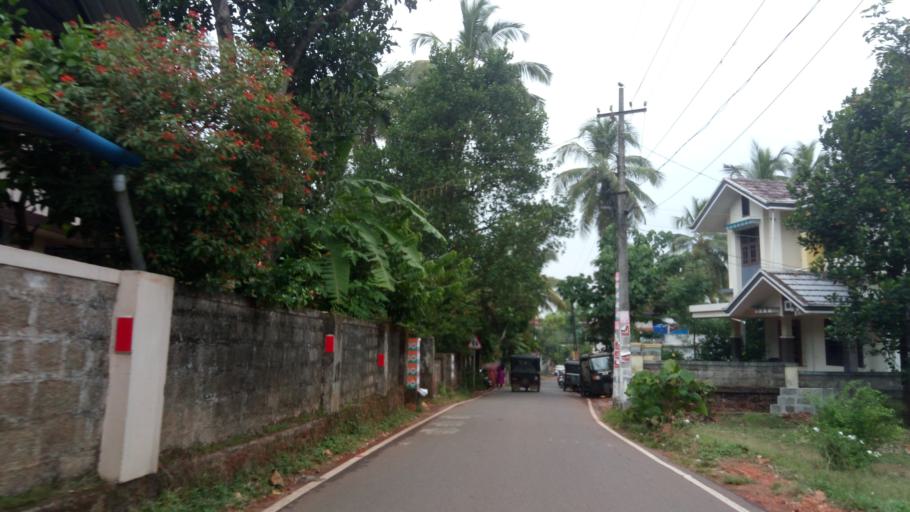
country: IN
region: Kerala
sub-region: Malappuram
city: Malappuram
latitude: 10.9908
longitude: 76.0079
